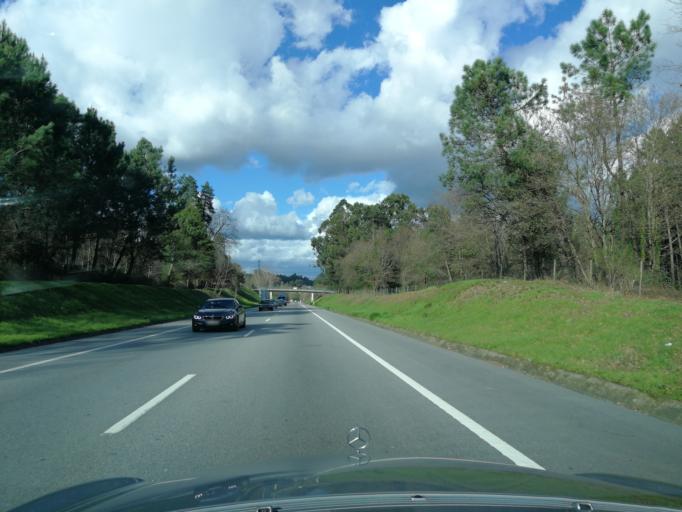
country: PT
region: Braga
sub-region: Vila Verde
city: Prado
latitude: 41.6115
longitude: -8.4554
